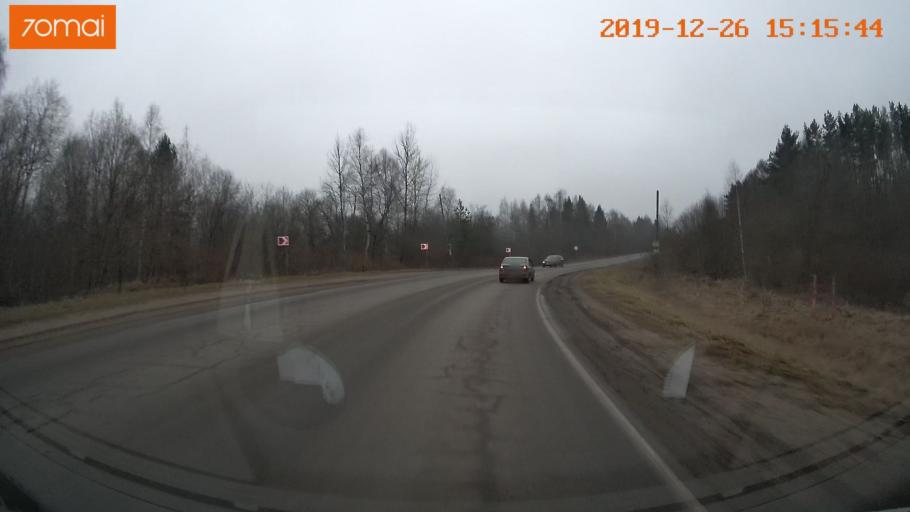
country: RU
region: Jaroslavl
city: Rybinsk
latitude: 58.0937
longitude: 38.8745
